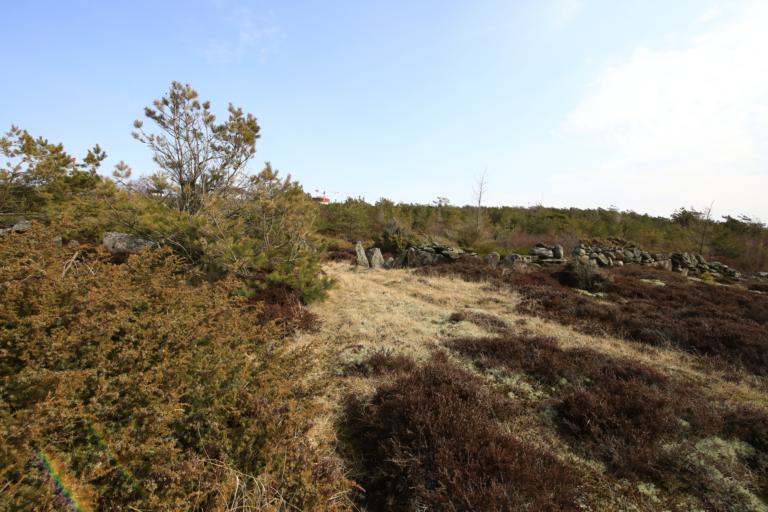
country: SE
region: Halland
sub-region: Kungsbacka Kommun
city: Frillesas
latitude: 57.2560
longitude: 12.0968
